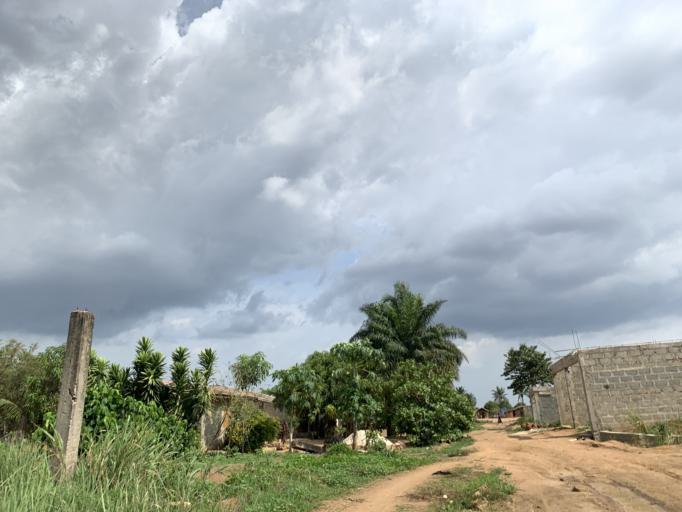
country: SL
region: Western Area
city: Waterloo
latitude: 8.3525
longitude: -13.0431
